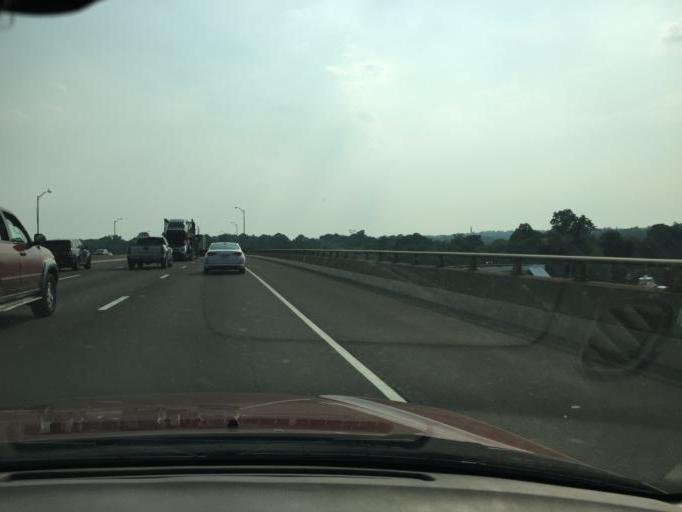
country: US
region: Connecticut
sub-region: Fairfield County
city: Cos Cob
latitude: 41.0367
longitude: -73.5919
